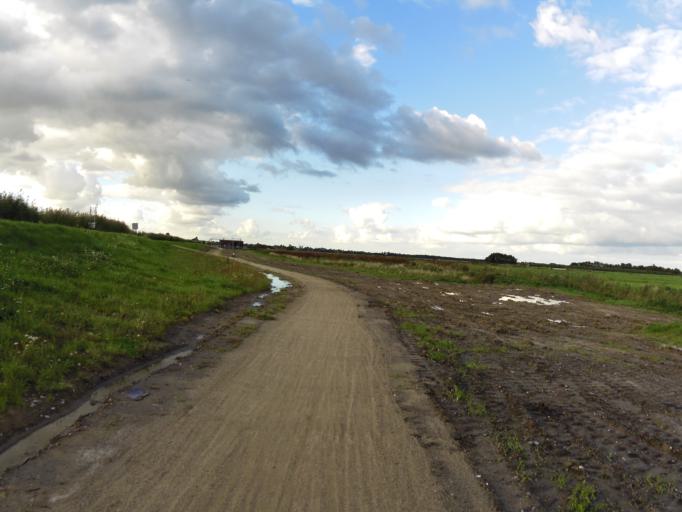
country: NL
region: Utrecht
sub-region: Gemeente Woerden
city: Woerden
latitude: 52.1390
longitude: 4.8730
